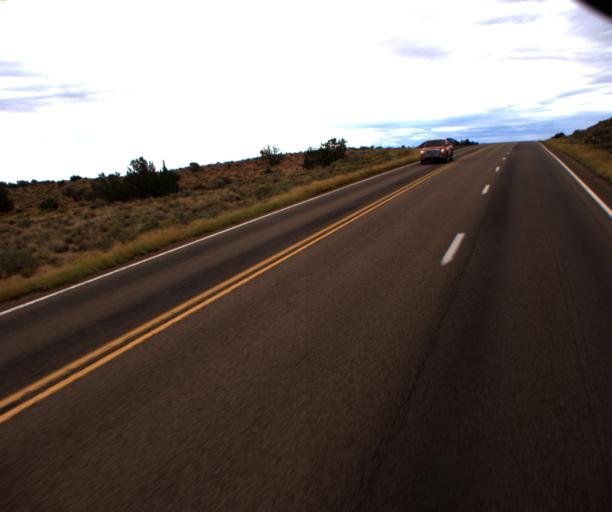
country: US
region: Arizona
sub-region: Navajo County
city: Snowflake
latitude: 34.6914
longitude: -110.1064
